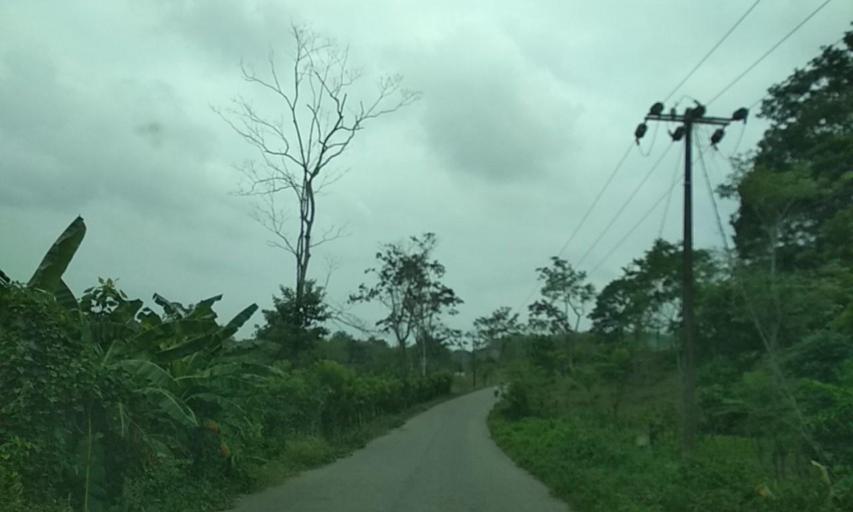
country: MX
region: Veracruz
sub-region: Uxpanapa
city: Poblado 10
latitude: 17.4641
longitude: -94.1088
